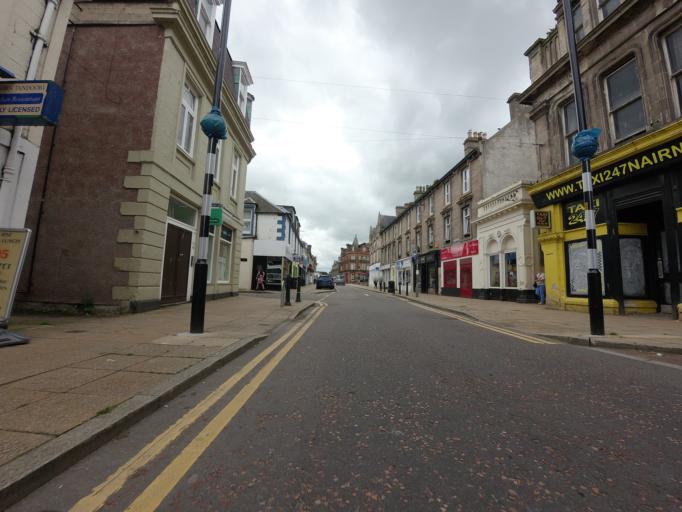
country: GB
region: Scotland
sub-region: Highland
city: Nairn
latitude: 57.5846
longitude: -3.8686
